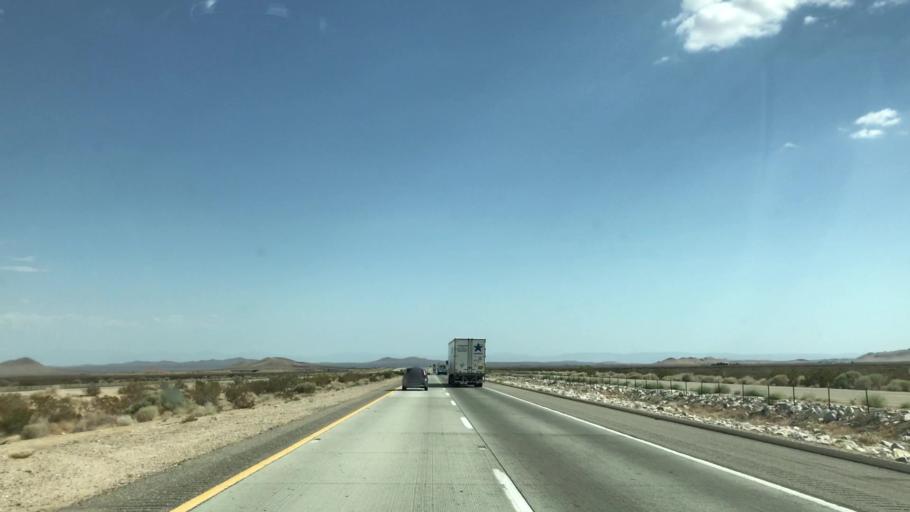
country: US
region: California
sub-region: Kern County
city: Mojave
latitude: 35.0613
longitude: -118.1131
